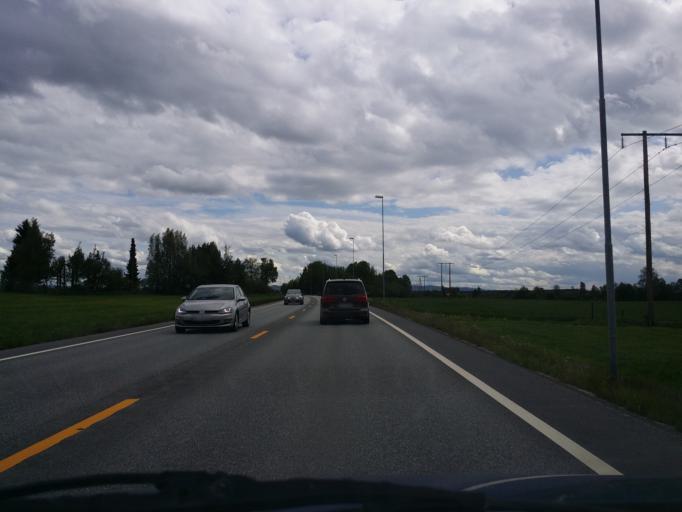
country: NO
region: Hedmark
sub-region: Stange
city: Stange
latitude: 60.7372
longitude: 11.2107
